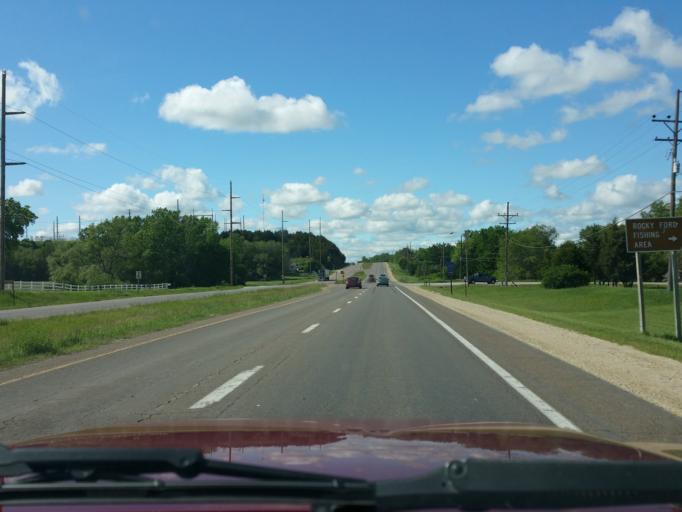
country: US
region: Kansas
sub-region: Riley County
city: Manhattan
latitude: 39.2282
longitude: -96.5838
